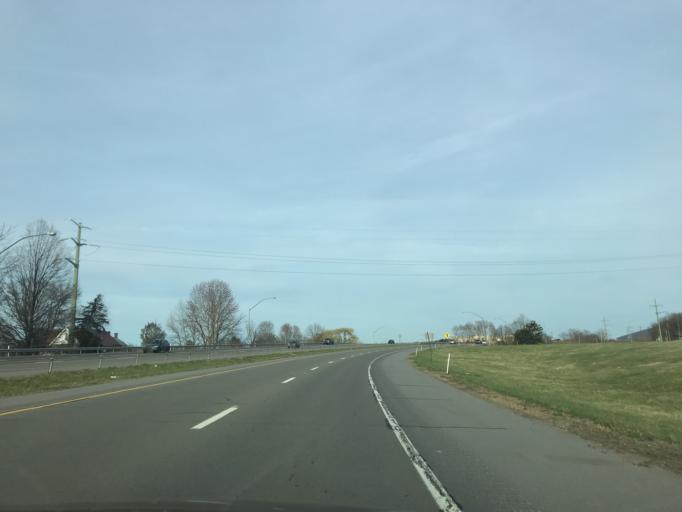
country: US
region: Pennsylvania
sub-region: Lycoming County
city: Faxon
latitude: 41.2488
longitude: -76.9804
